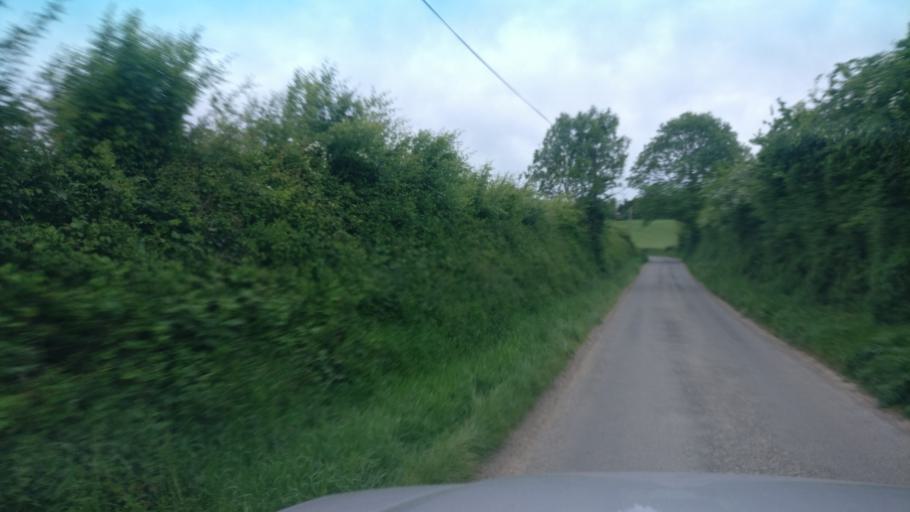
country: IE
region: Connaught
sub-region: County Galway
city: Portumna
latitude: 53.1349
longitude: -8.2916
